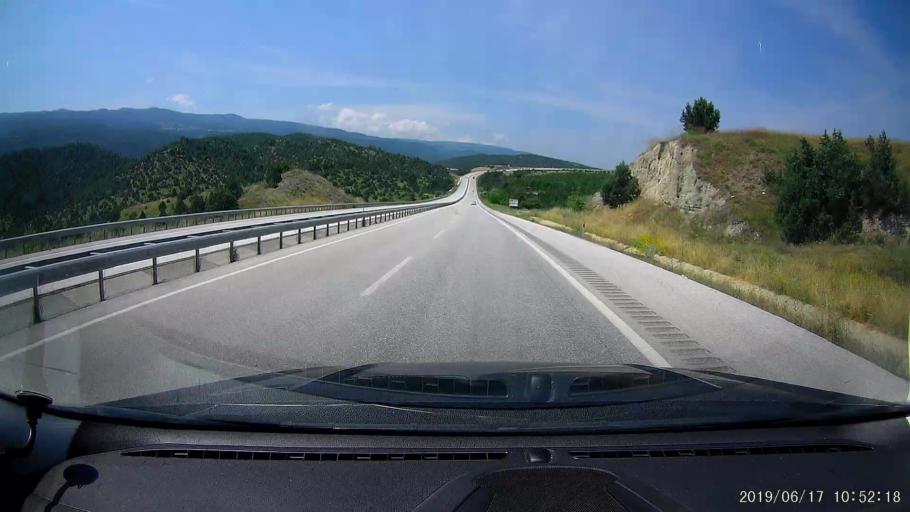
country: TR
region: Corum
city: Hacihamza
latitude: 41.0915
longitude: 34.3442
